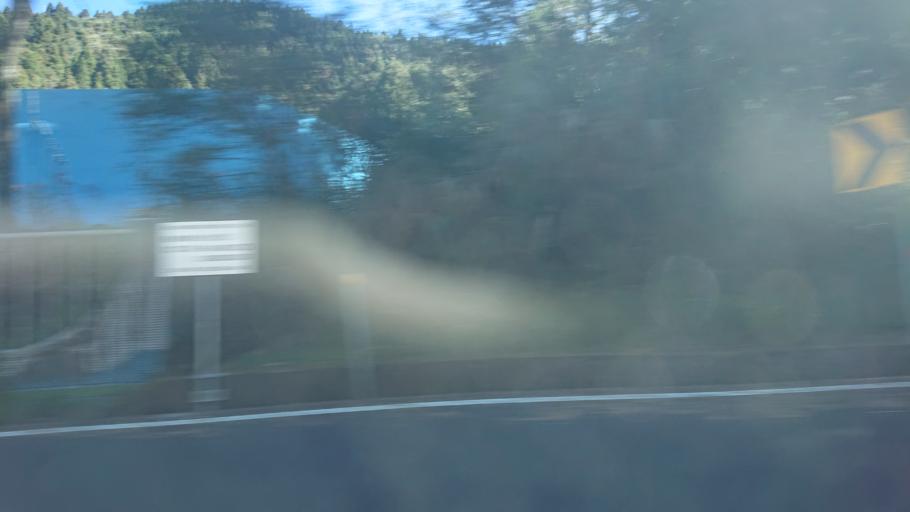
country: TW
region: Taiwan
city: Lugu
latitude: 23.4944
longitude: 120.8206
